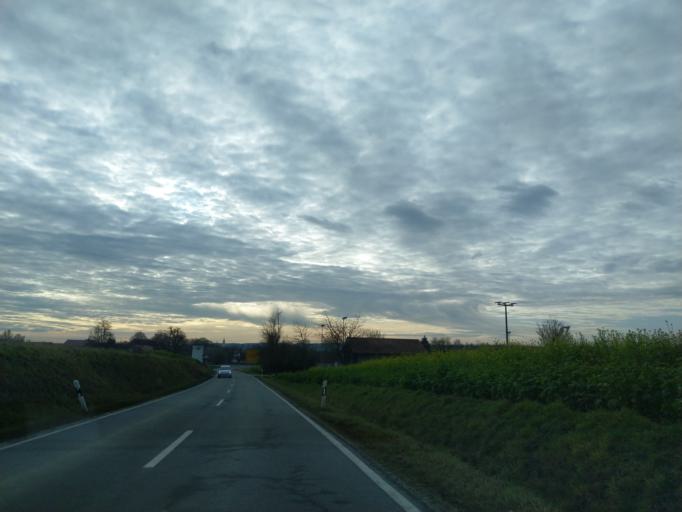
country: DE
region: Bavaria
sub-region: Lower Bavaria
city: Buchhofen
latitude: 48.7012
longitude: 12.9418
